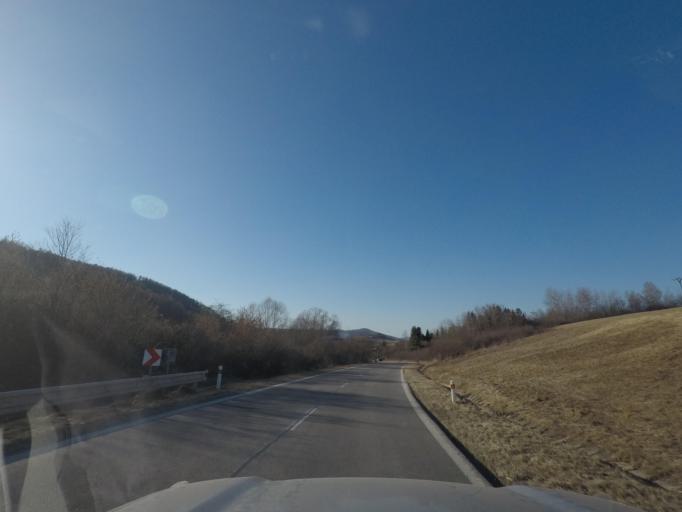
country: SK
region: Presovsky
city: Medzilaborce
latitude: 49.2425
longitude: 21.9373
